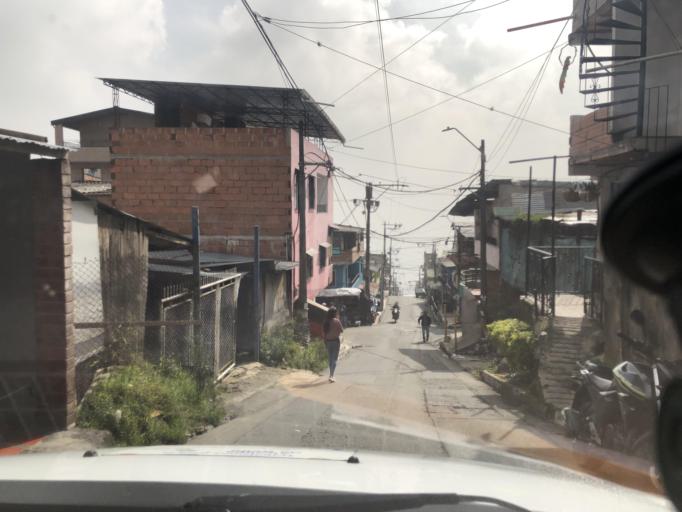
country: CO
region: Antioquia
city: Bello
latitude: 6.3150
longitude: -75.5853
